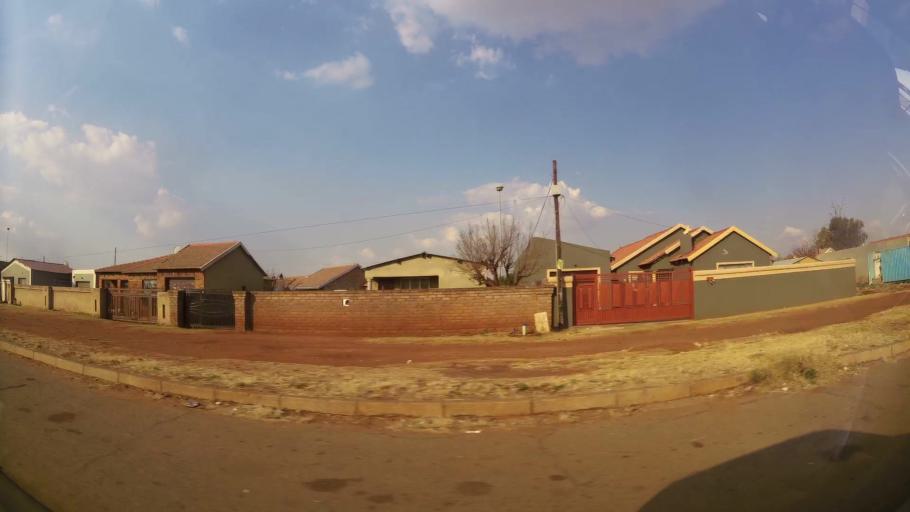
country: ZA
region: Gauteng
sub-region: Ekurhuleni Metropolitan Municipality
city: Germiston
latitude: -26.3634
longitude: 28.1882
